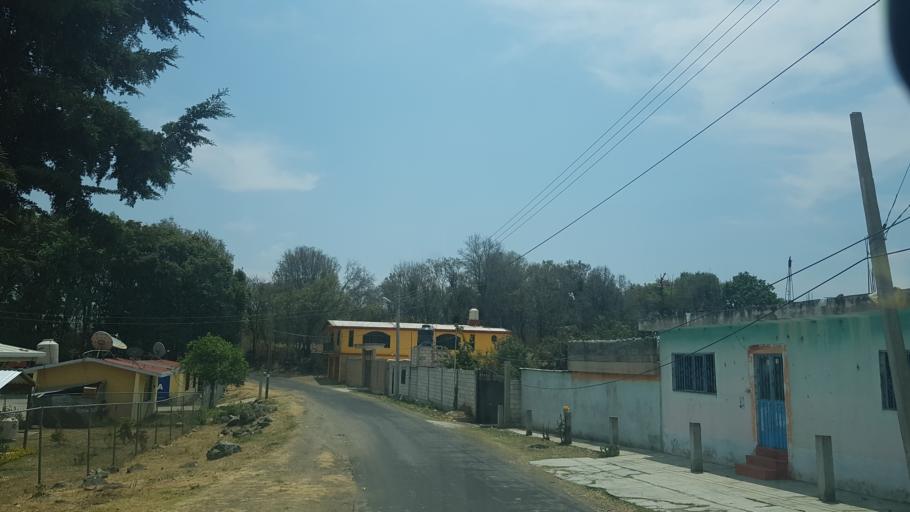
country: MX
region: Puebla
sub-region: Tochimilco
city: La Magdalena Yancuitlalpan
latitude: 18.8873
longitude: -98.6018
